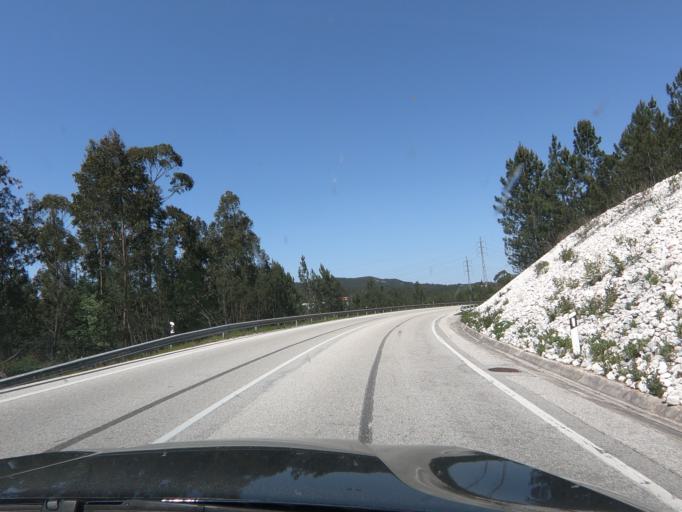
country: PT
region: Coimbra
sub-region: Miranda do Corvo
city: Miranda do Corvo
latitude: 40.0950
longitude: -8.3158
